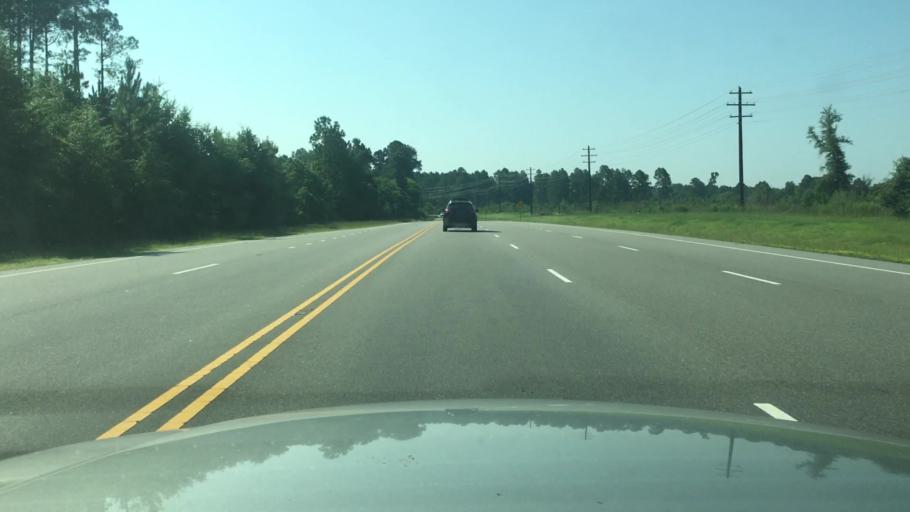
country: US
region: North Carolina
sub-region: Cumberland County
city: Spring Lake
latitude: 35.1369
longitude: -78.9042
